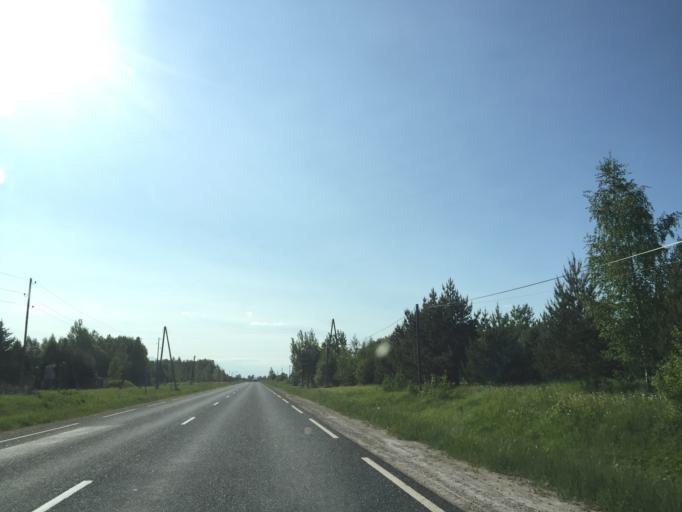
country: LV
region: Salaspils
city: Salaspils
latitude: 56.8237
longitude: 24.3832
